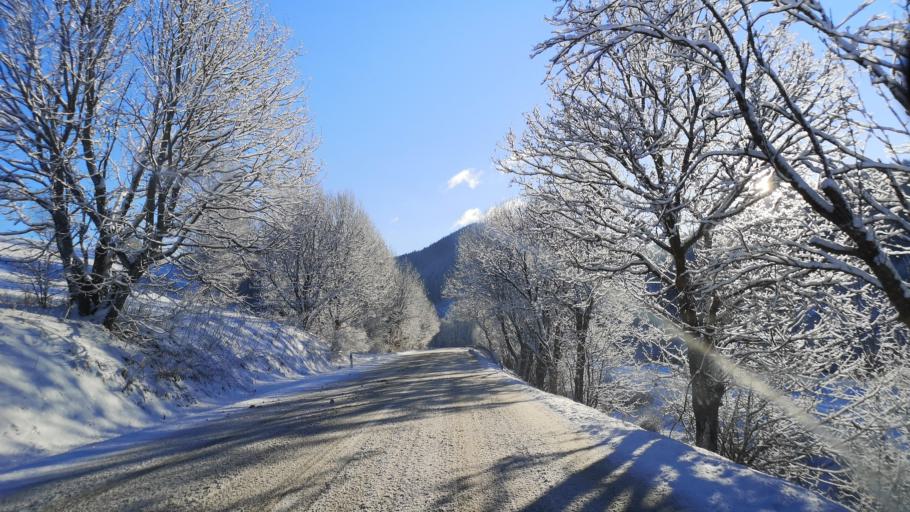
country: SK
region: Banskobystricky
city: Revuca
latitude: 48.8299
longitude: 20.0826
